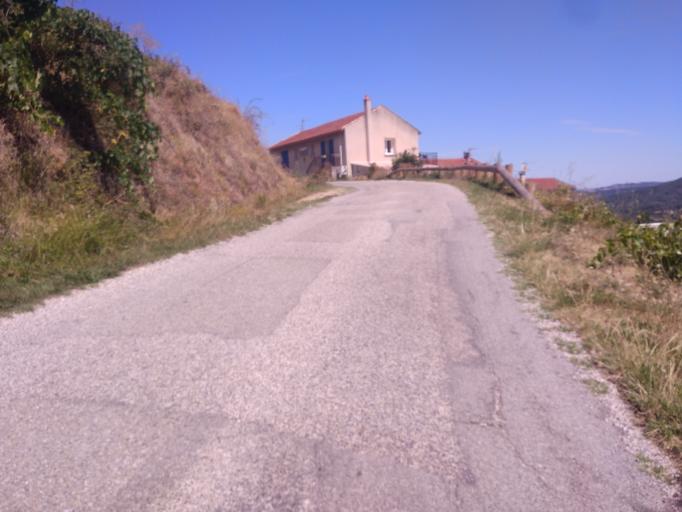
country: FR
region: Rhone-Alpes
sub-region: Departement de l'Ardeche
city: Sarras
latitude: 45.1842
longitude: 4.7911
